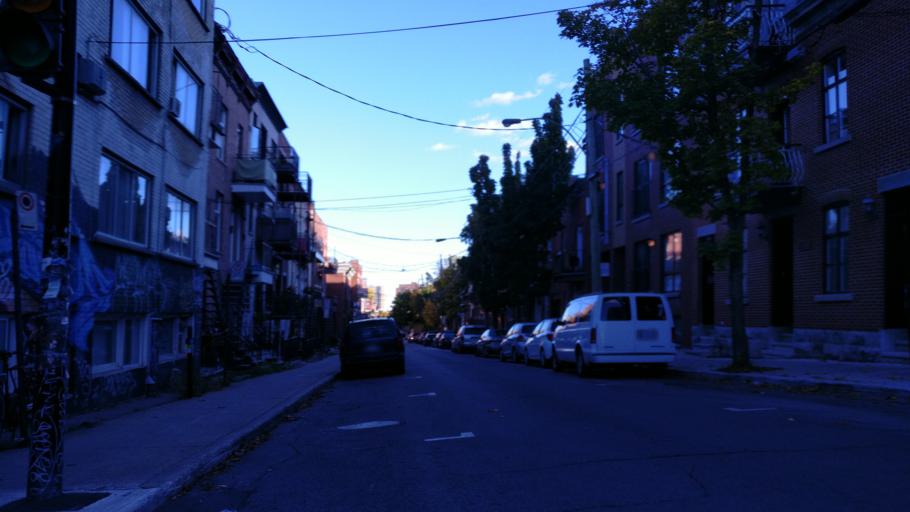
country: CA
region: Quebec
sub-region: Montreal
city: Montreal
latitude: 45.5189
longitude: -73.5808
